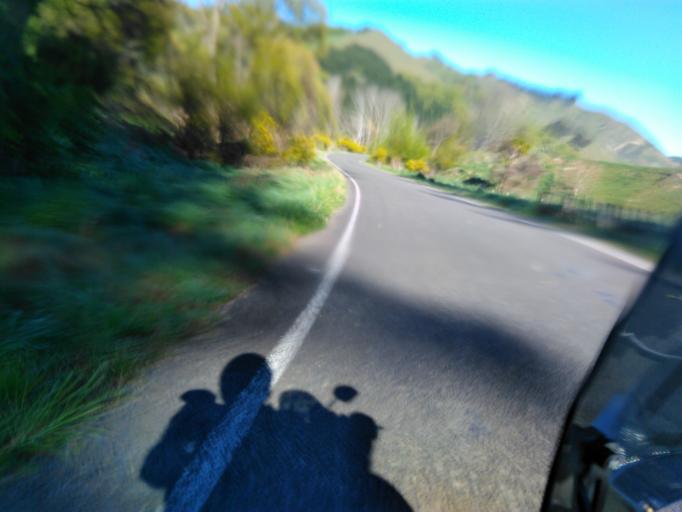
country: NZ
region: Gisborne
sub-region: Gisborne District
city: Gisborne
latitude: -38.4435
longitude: 177.7595
